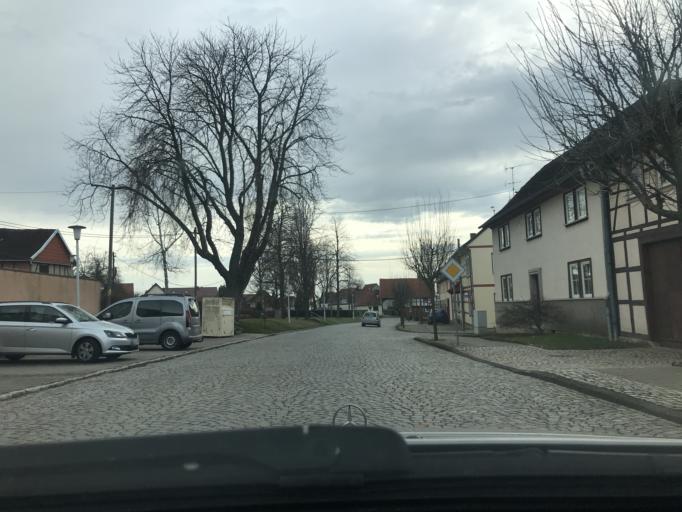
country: DE
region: Thuringia
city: Niederdorla
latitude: 51.1610
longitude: 10.4495
